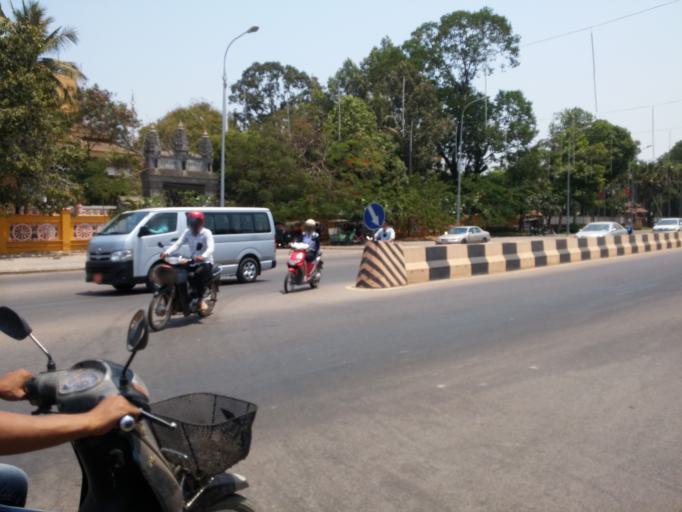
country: KH
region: Siem Reap
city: Siem Reap
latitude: 13.3640
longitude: 103.8546
